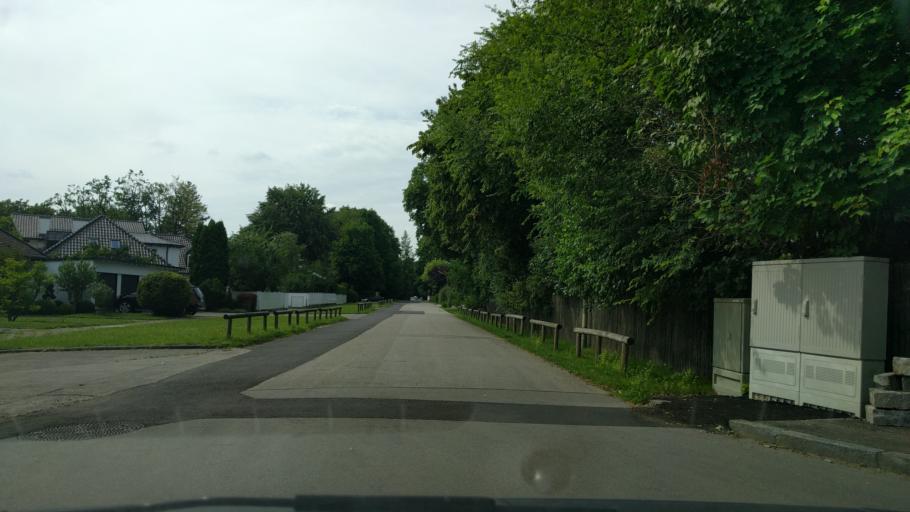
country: DE
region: Bavaria
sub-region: Upper Bavaria
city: Pullach im Isartal
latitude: 48.0583
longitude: 11.5469
